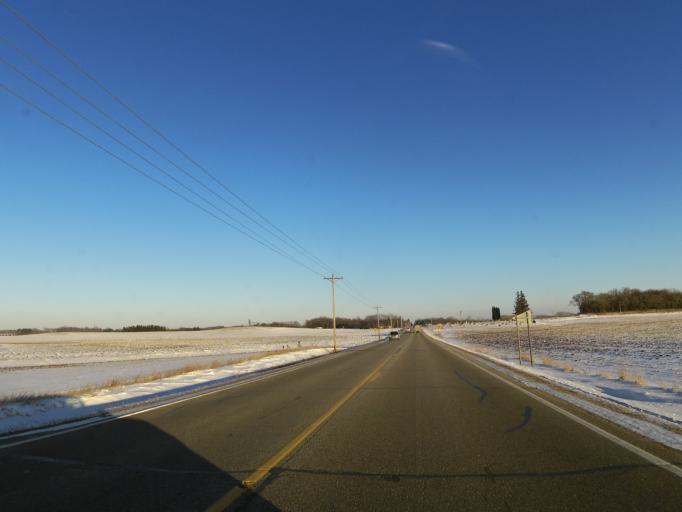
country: US
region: Minnesota
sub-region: Rice County
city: Northfield
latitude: 44.5440
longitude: -93.1702
